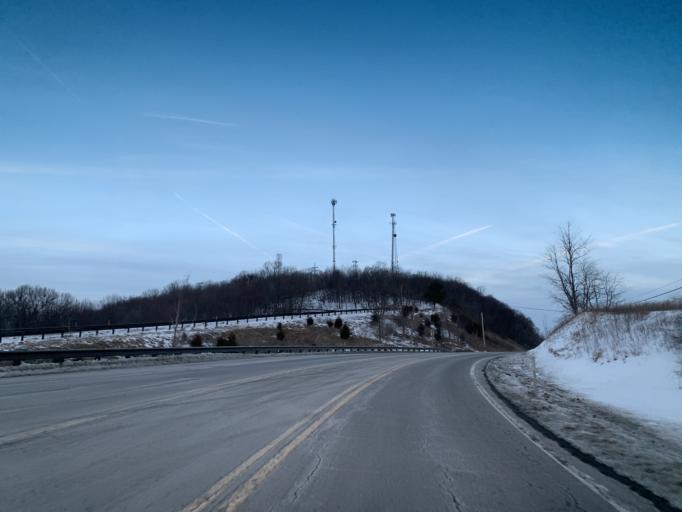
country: US
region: Maryland
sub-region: Allegany County
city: Cumberland
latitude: 39.7047
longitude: -78.6301
